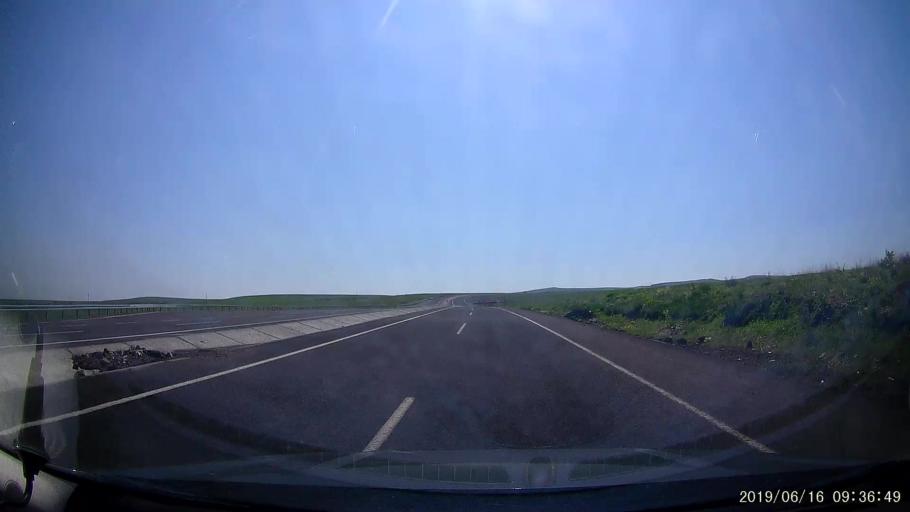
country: TR
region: Kars
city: Kars
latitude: 40.5557
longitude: 43.1806
